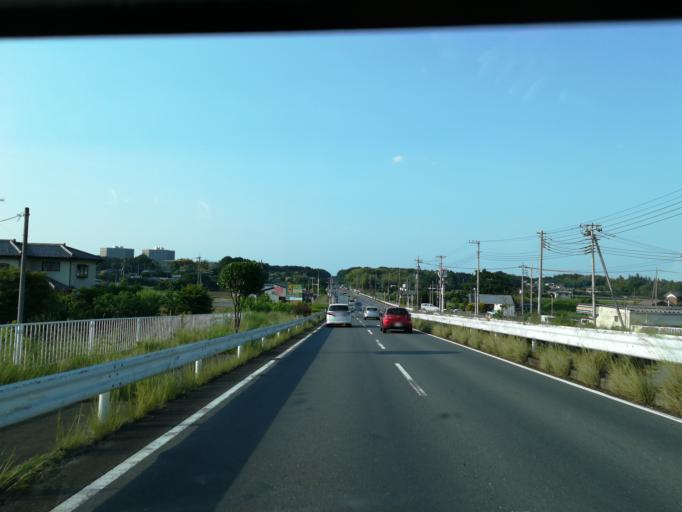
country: JP
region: Saitama
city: Kumagaya
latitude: 36.0966
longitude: 139.3638
